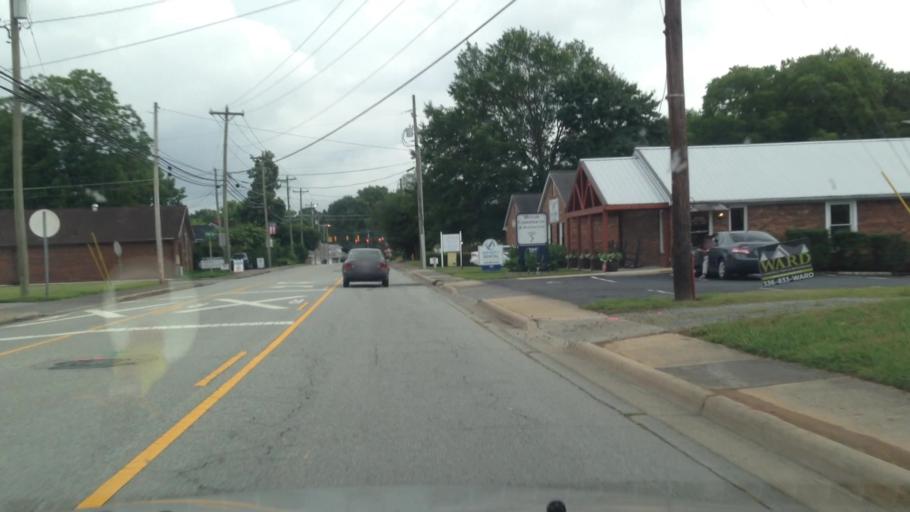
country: US
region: North Carolina
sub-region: Forsyth County
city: Kernersville
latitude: 36.1222
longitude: -80.0731
